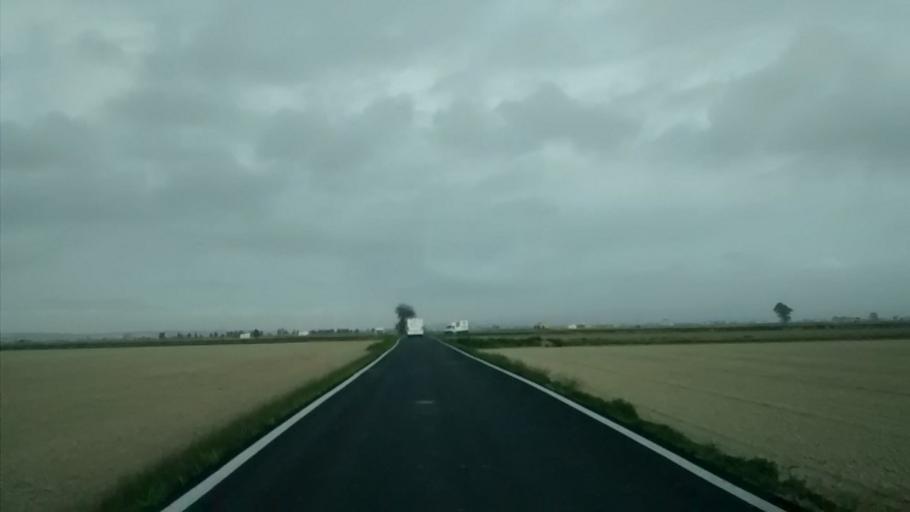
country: ES
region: Catalonia
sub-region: Provincia de Tarragona
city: Deltebre
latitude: 40.6702
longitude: 0.6525
